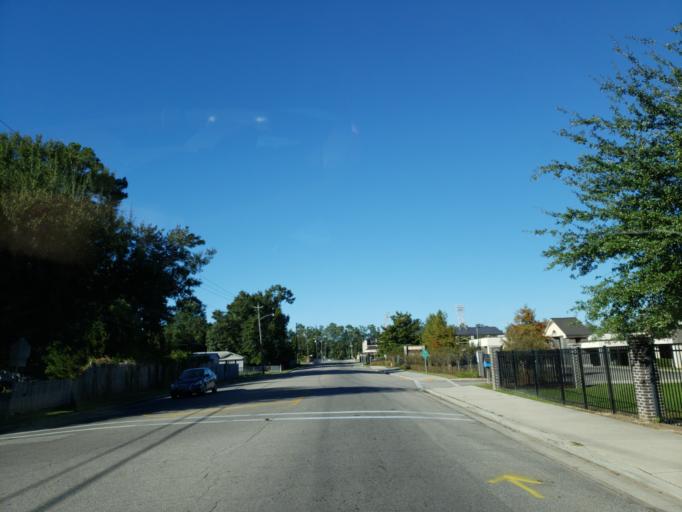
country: US
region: Mississippi
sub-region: Forrest County
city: Hattiesburg
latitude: 31.3283
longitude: -89.3100
